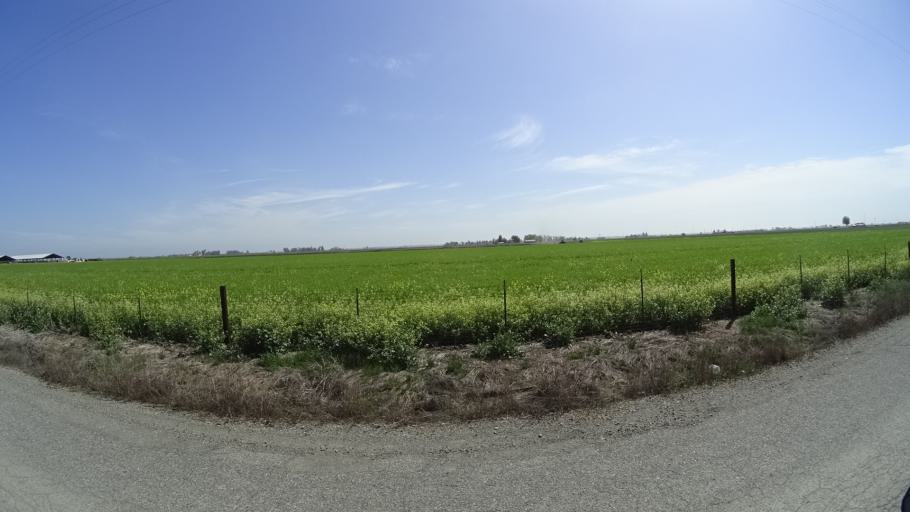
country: US
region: California
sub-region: Glenn County
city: Willows
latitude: 39.5883
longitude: -122.0886
